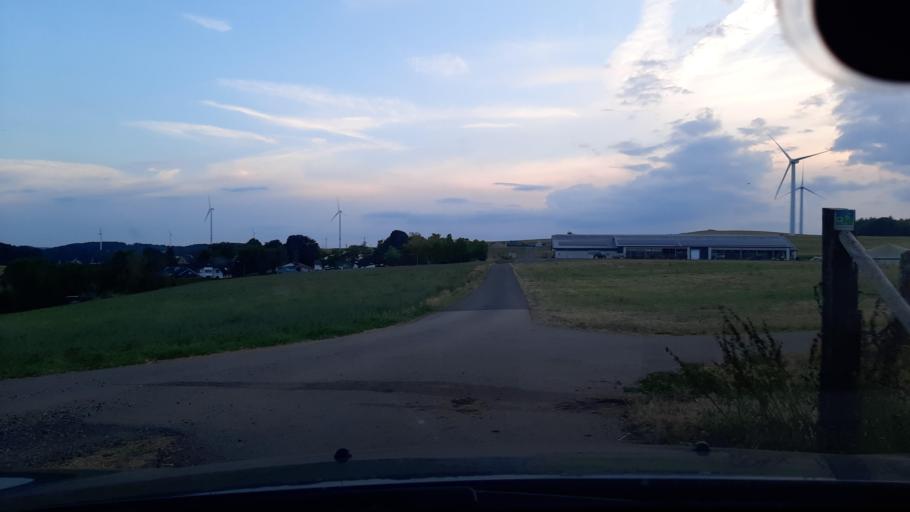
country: DE
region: North Rhine-Westphalia
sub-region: Regierungsbezirk Koln
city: Mechernich
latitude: 50.5634
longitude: 6.6364
